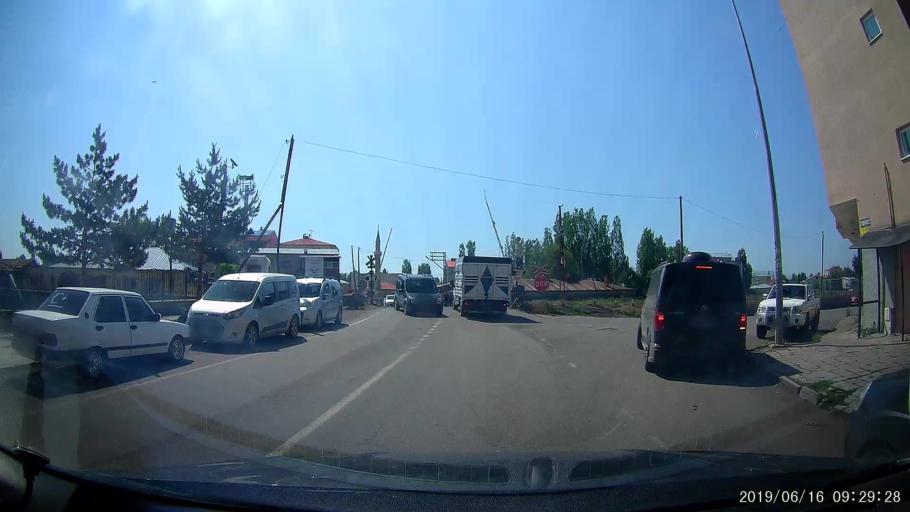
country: TR
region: Kars
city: Kars
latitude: 40.6017
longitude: 43.1040
